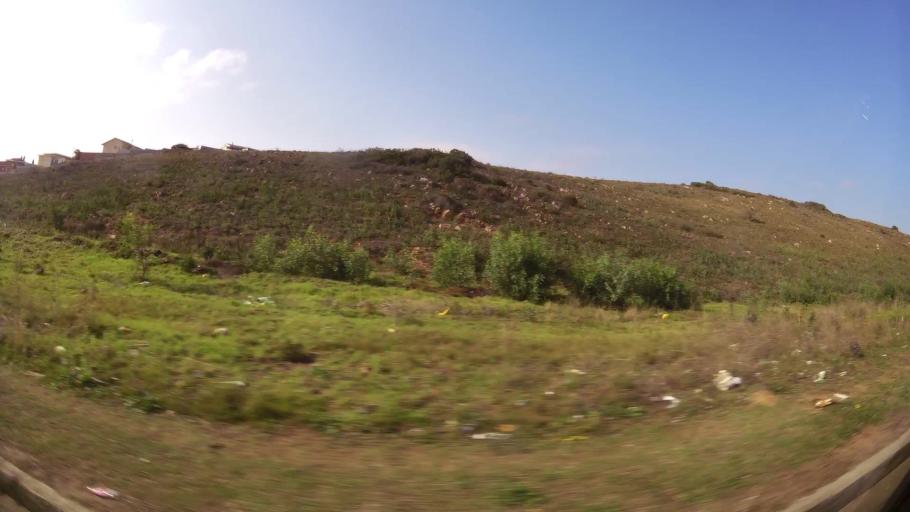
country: ZA
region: Eastern Cape
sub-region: Nelson Mandela Bay Metropolitan Municipality
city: Port Elizabeth
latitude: -33.9252
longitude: 25.5491
